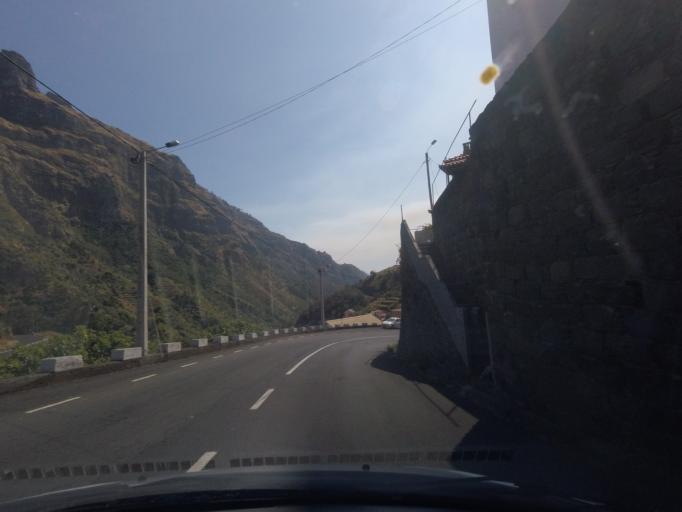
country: PT
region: Madeira
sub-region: Camara de Lobos
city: Curral das Freiras
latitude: 32.7303
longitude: -17.0280
